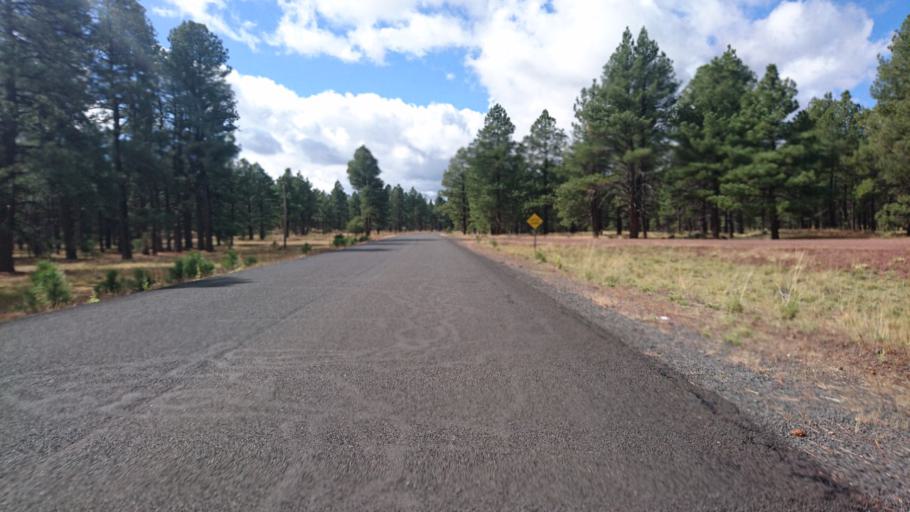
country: US
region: Arizona
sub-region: Coconino County
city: Parks
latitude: 35.2600
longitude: -111.9302
